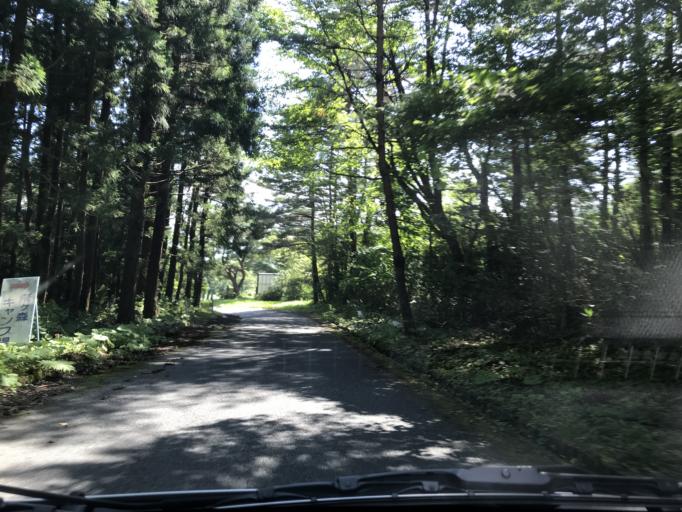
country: JP
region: Iwate
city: Ichinoseki
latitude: 38.9756
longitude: 141.4246
